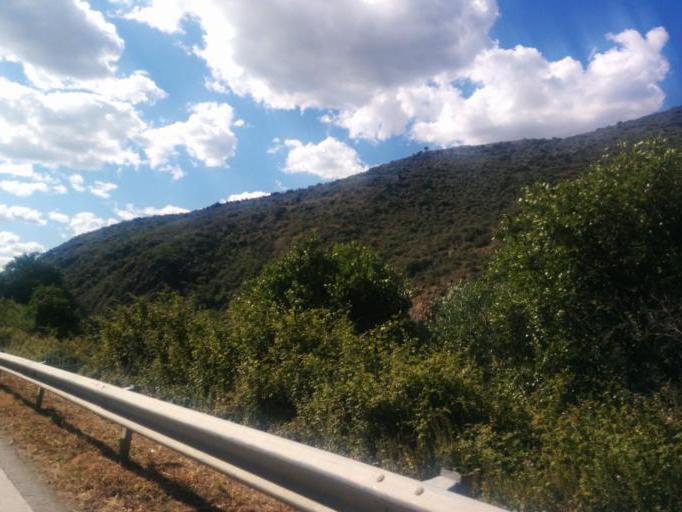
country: PT
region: Viseu
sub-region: Armamar
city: Armamar
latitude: 41.1432
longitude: -7.7132
